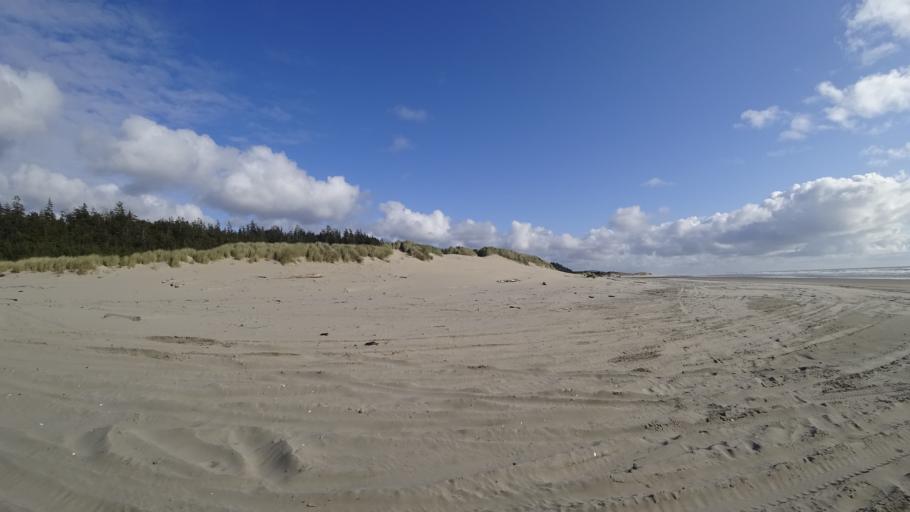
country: US
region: Oregon
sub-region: Douglas County
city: Reedsport
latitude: 43.7485
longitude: -124.1823
